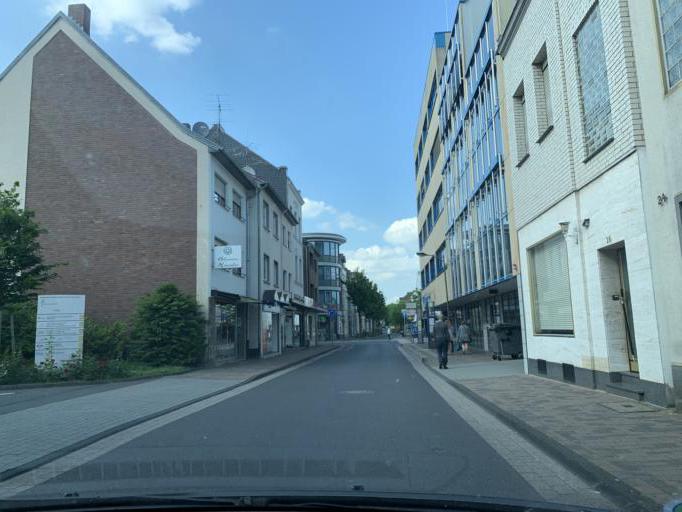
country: DE
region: North Rhine-Westphalia
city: Bruhl
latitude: 50.8276
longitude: 6.9020
